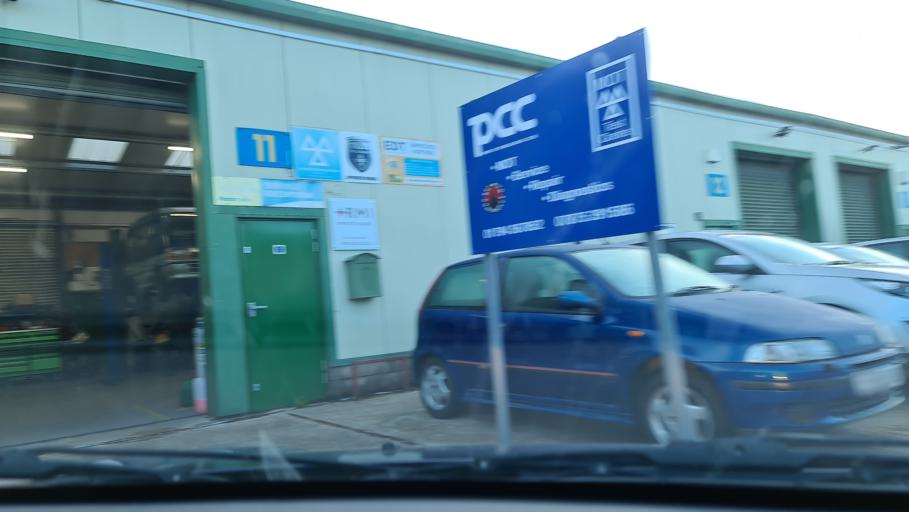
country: GB
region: England
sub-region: Hampshire
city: Romsey
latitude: 51.0130
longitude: -1.4902
